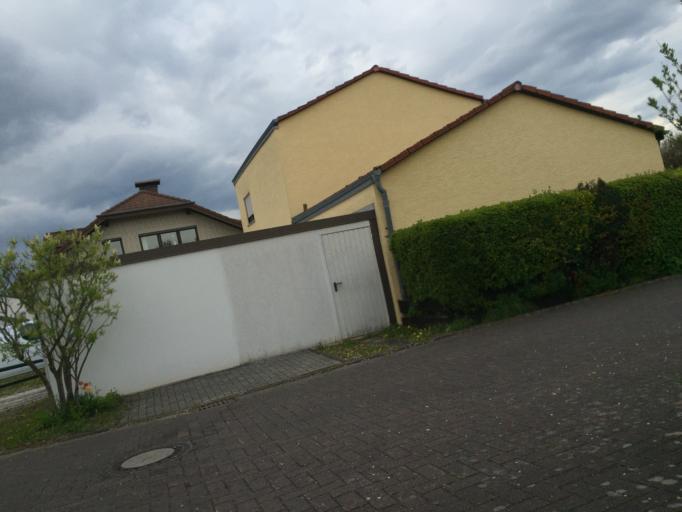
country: DE
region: North Rhine-Westphalia
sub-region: Regierungsbezirk Koln
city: Alfter
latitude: 50.7537
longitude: 7.0423
